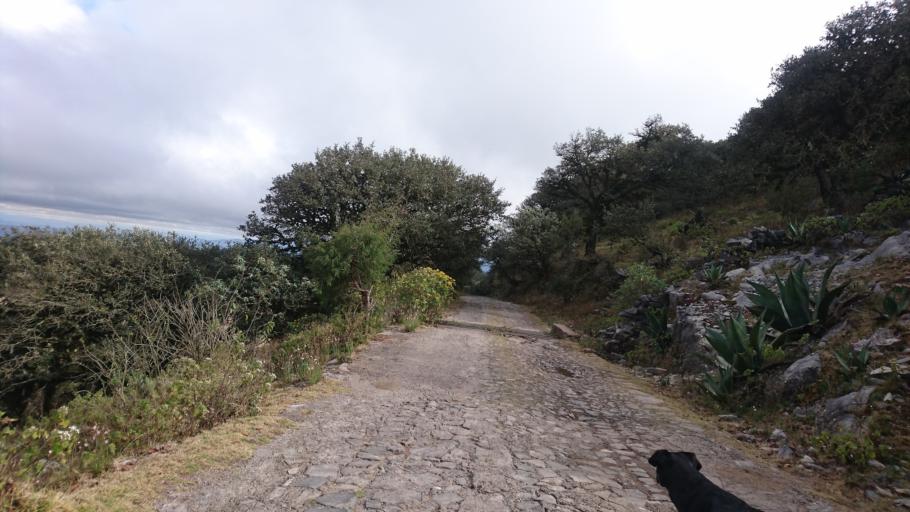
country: MX
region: San Luis Potosi
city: Zaragoza
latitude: 22.0752
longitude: -100.6404
